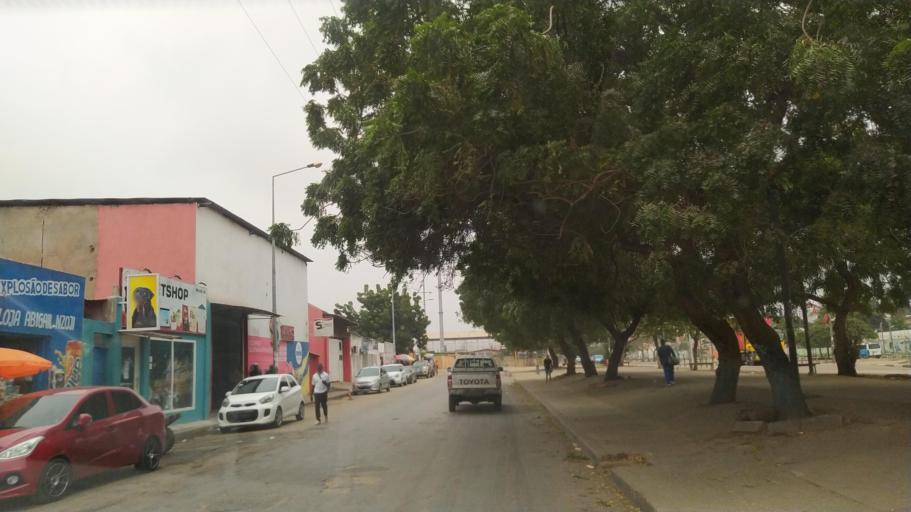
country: AO
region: Luanda
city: Luanda
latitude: -8.8317
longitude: 13.2503
